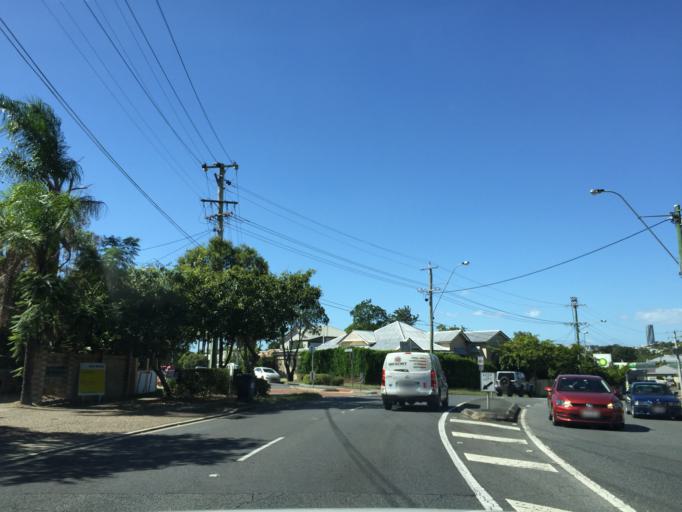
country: AU
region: Queensland
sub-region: Brisbane
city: Milton
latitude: -27.4455
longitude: 152.9962
